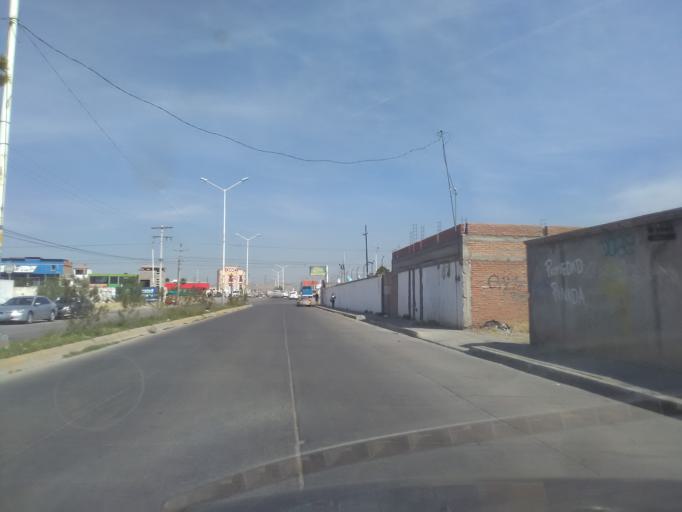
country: MX
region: Durango
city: Victoria de Durango
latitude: 24.0553
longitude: -104.6284
